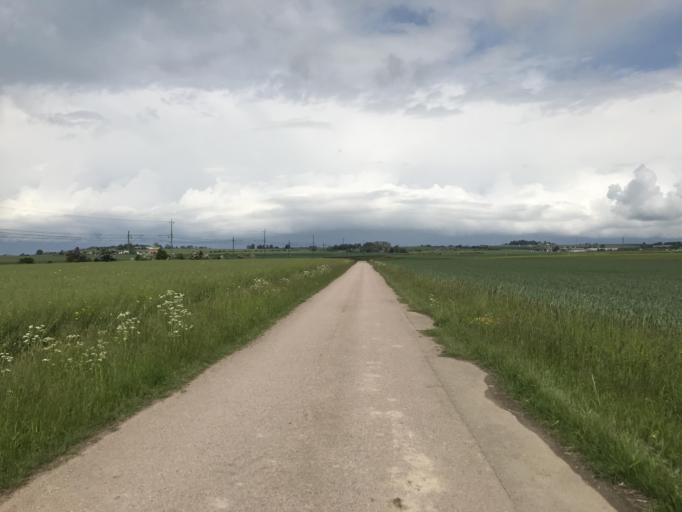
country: SE
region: Skane
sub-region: Landskrona
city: Landskrona
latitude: 55.9079
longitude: 12.8448
